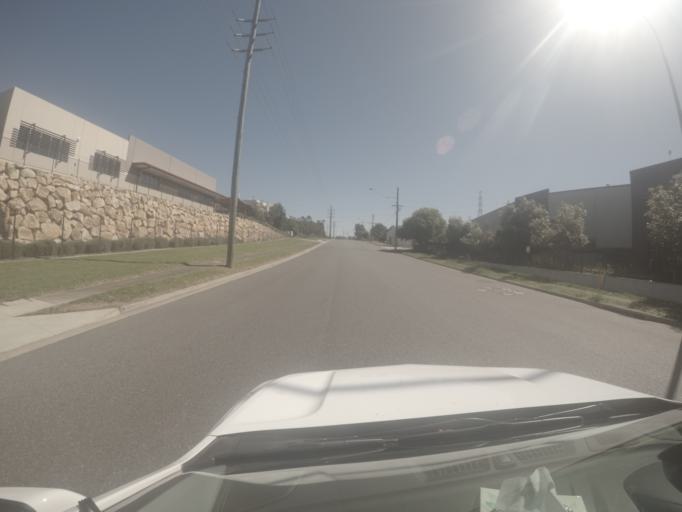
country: AU
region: Queensland
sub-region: Brisbane
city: Richlands
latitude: -27.5801
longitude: 152.9508
